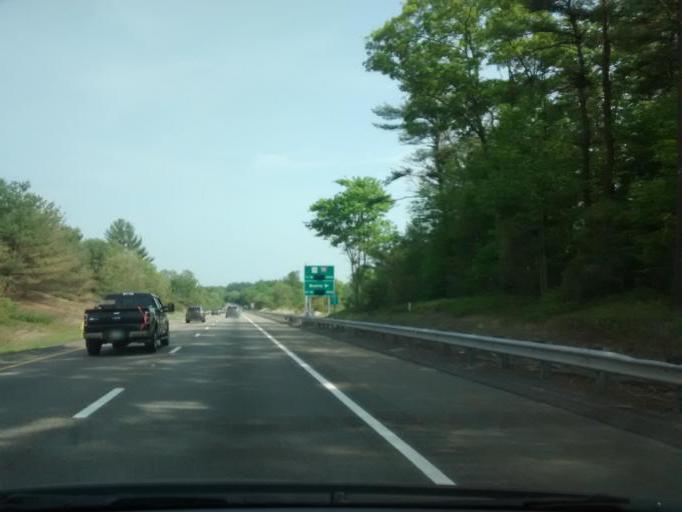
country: US
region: Massachusetts
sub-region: Bristol County
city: Raynham Center
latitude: 41.9267
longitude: -71.0007
